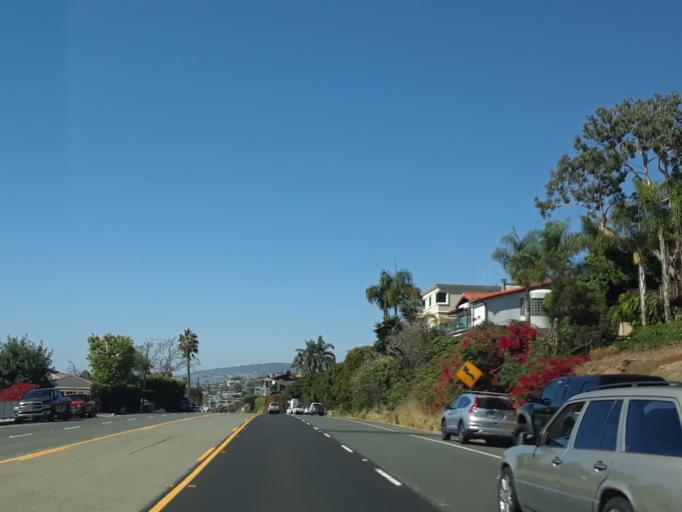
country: US
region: California
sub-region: Orange County
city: Laguna Niguel
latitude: 33.5064
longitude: -117.7478
